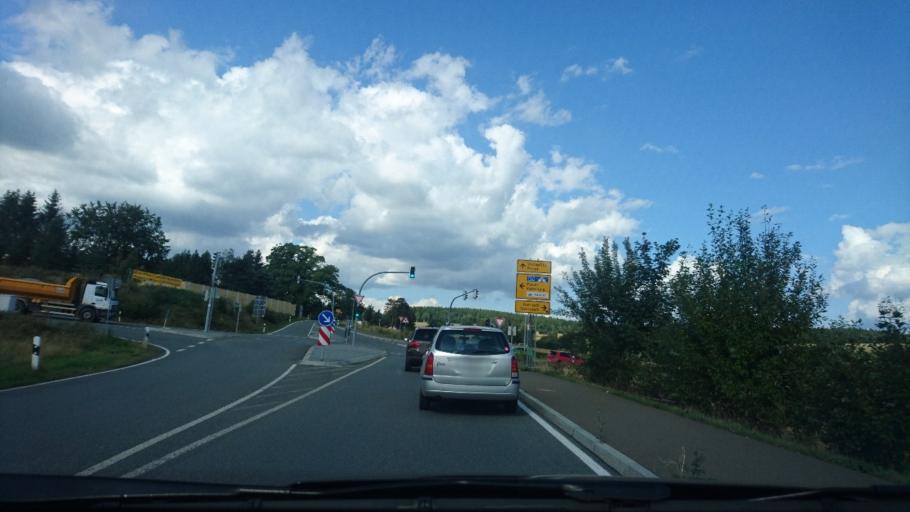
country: DE
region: Saxony
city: Treuen
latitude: 50.5457
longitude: 12.3142
